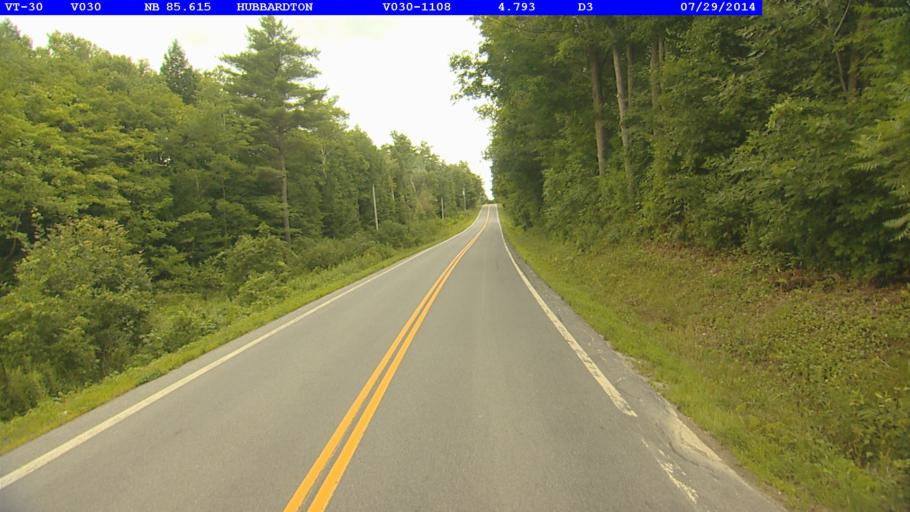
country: US
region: Vermont
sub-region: Rutland County
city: Brandon
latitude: 43.7453
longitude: -73.1868
